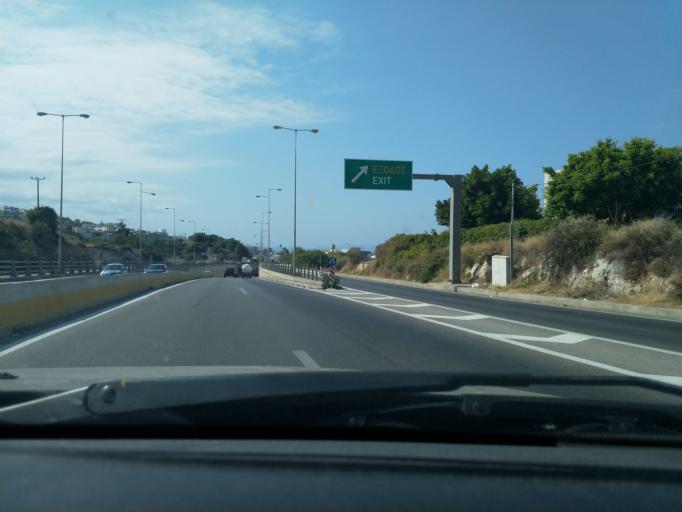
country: GR
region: Crete
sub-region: Nomos Rethymnis
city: Atsipopoulon
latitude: 35.3607
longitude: 24.4474
